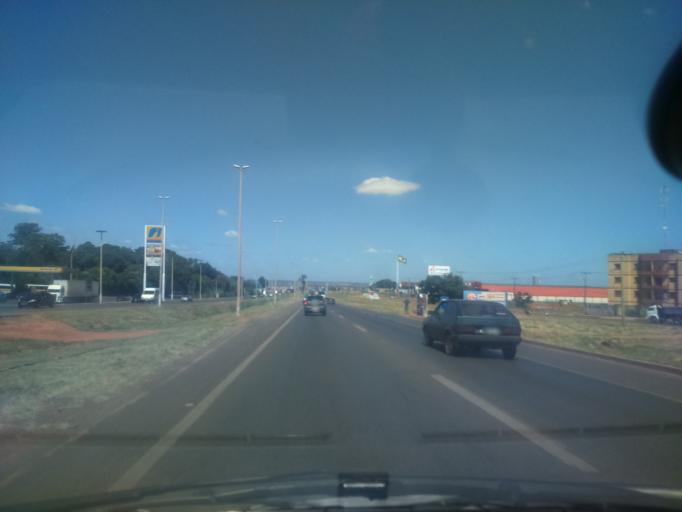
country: BR
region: Goias
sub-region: Luziania
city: Luziania
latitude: -16.0899
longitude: -47.9843
